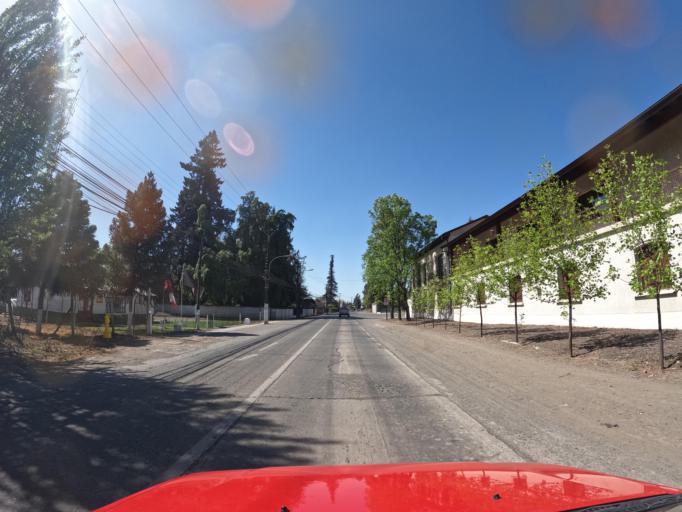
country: CL
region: Maule
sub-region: Provincia de Curico
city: Molina
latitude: -35.0783
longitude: -71.2605
